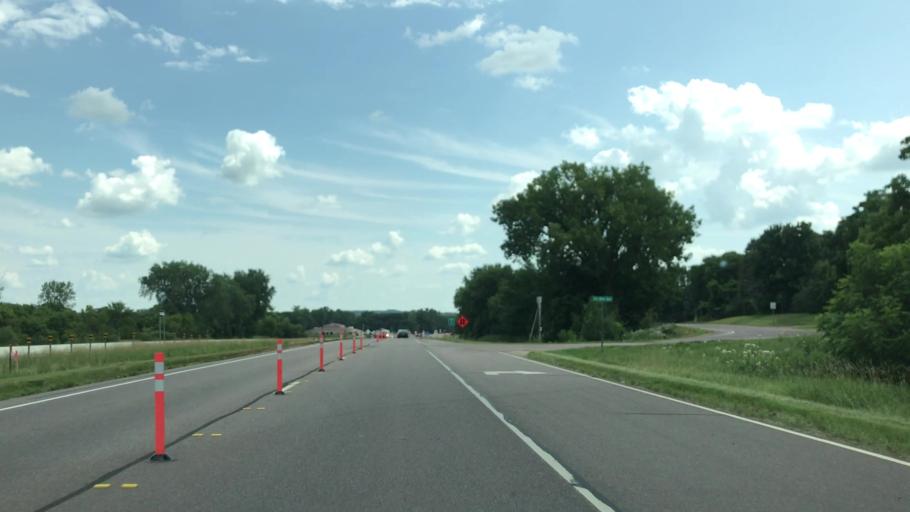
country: US
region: Minnesota
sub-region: Nicollet County
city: Saint Peter
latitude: 44.3545
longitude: -93.9549
